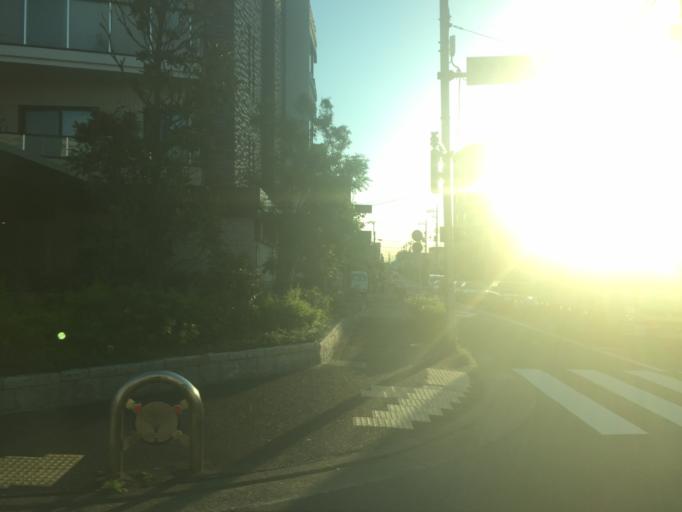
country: JP
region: Tokyo
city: Tokyo
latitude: 35.6217
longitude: 139.6400
